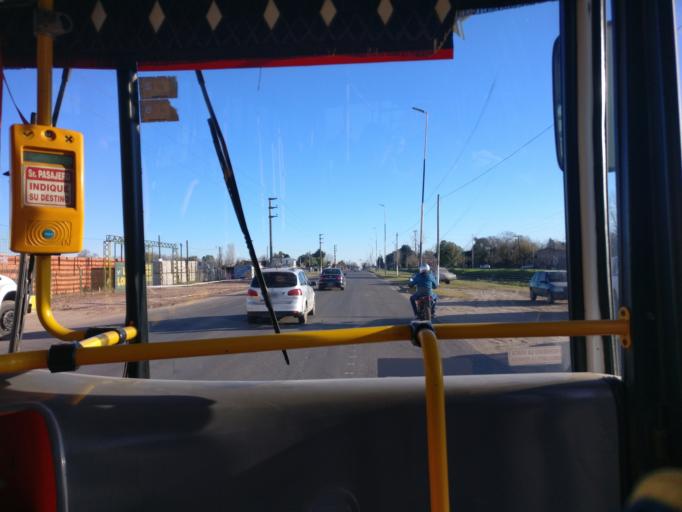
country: AR
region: Buenos Aires
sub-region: Partido de Ezeiza
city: Ezeiza
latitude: -34.8944
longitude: -58.5741
